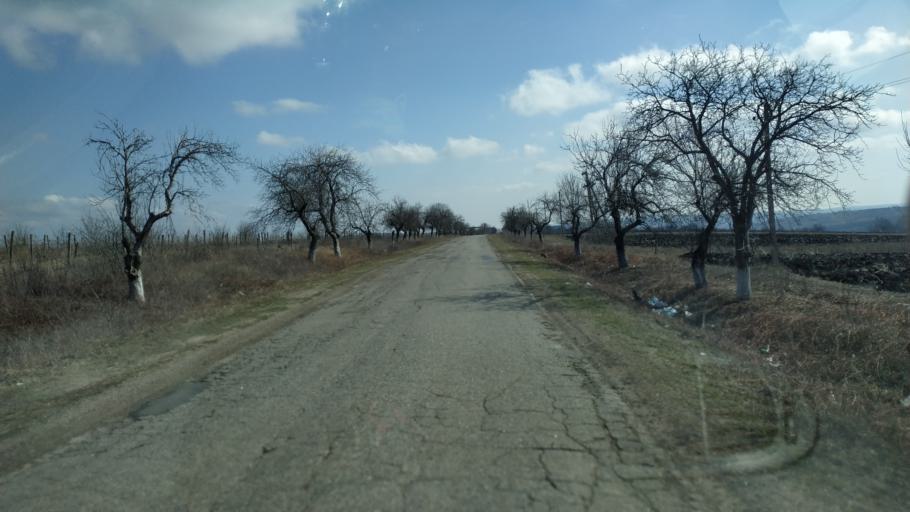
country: MD
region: Hincesti
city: Hincesti
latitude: 46.8510
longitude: 28.6481
